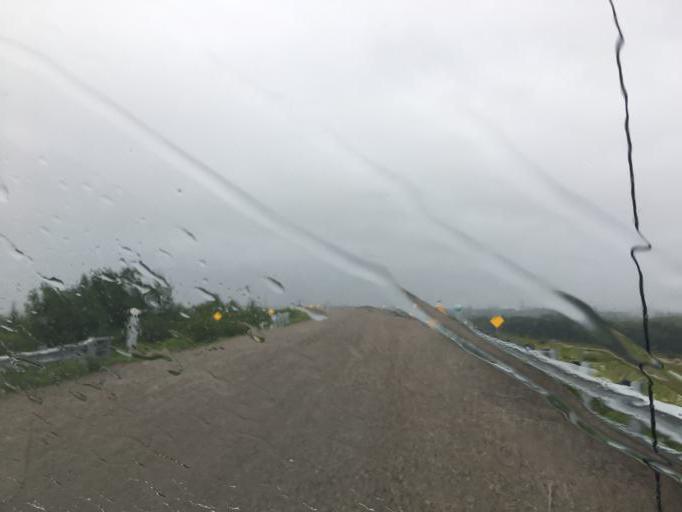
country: CA
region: Ontario
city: Kitchener
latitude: 43.4369
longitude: -80.5716
